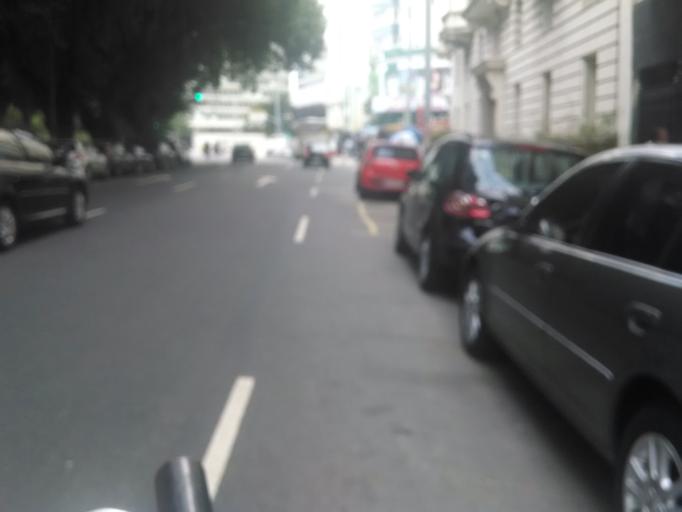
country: BR
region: Rio de Janeiro
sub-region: Rio De Janeiro
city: Rio de Janeiro
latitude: -22.9408
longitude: -43.1779
